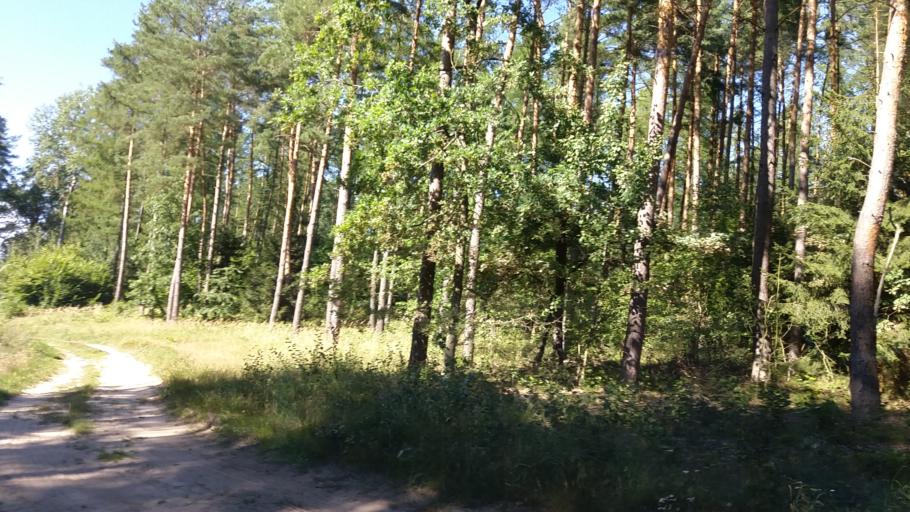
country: PL
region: West Pomeranian Voivodeship
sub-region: Powiat choszczenski
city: Krzecin
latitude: 53.0893
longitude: 15.4463
